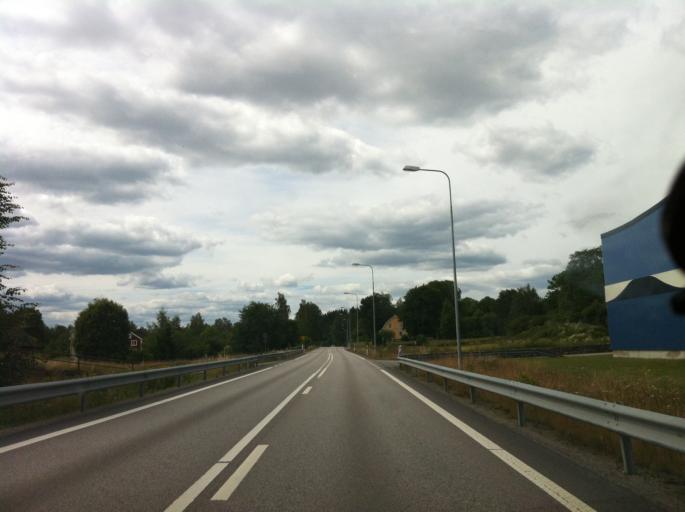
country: SE
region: Kronoberg
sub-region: Tingsryds Kommun
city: Tingsryd
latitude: 56.4995
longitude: 15.0528
